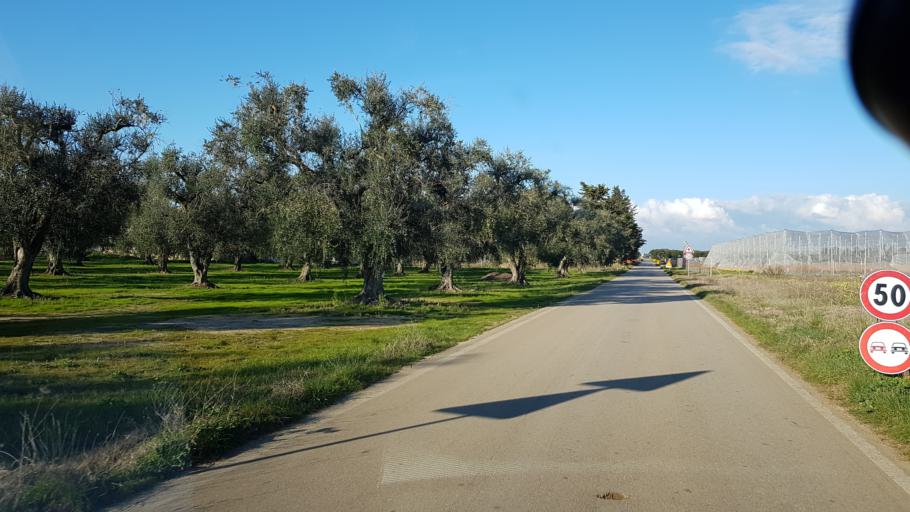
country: IT
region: Apulia
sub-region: Provincia di Brindisi
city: Tuturano
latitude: 40.5661
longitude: 17.8984
